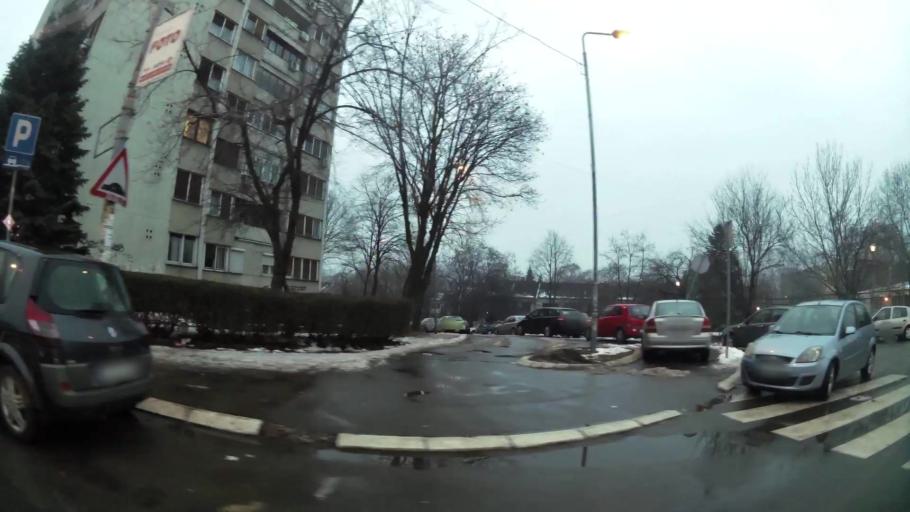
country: RS
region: Central Serbia
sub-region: Belgrade
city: Vozdovac
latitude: 44.7687
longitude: 20.4984
